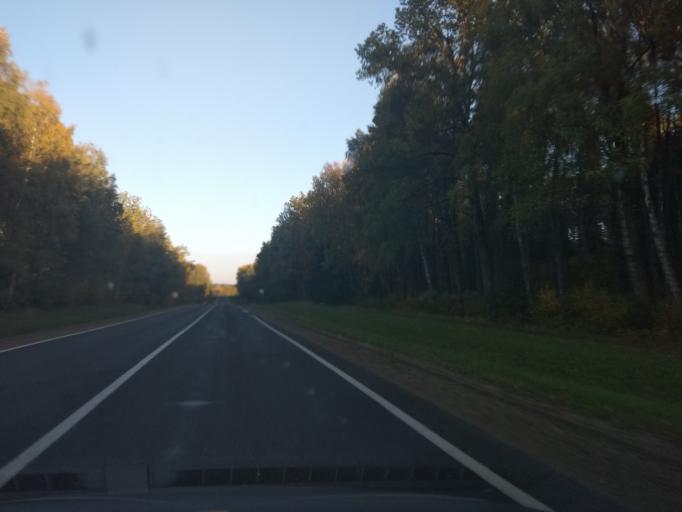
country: BY
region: Grodnenskaya
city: Vawkavysk
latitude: 53.1462
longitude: 24.5998
